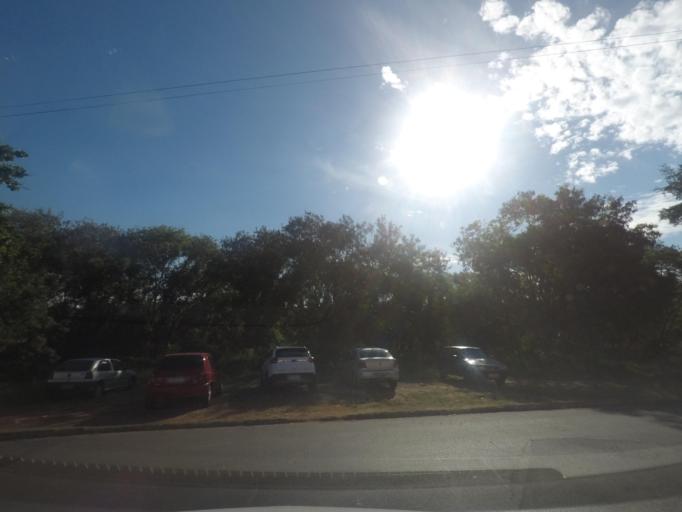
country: BR
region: Sao Paulo
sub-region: Sumare
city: Sumare
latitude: -22.8135
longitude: -47.2668
